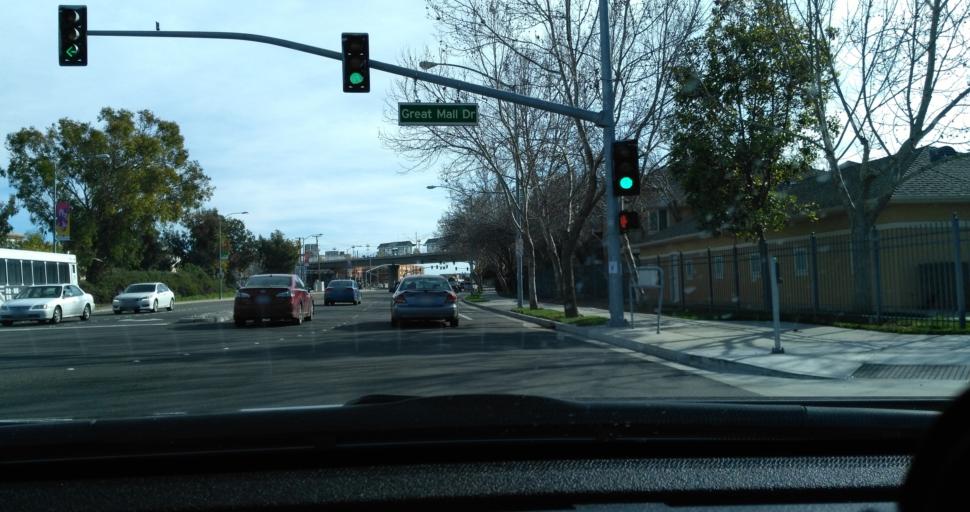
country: US
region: California
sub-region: Santa Clara County
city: Milpitas
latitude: 37.4165
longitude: -121.9028
